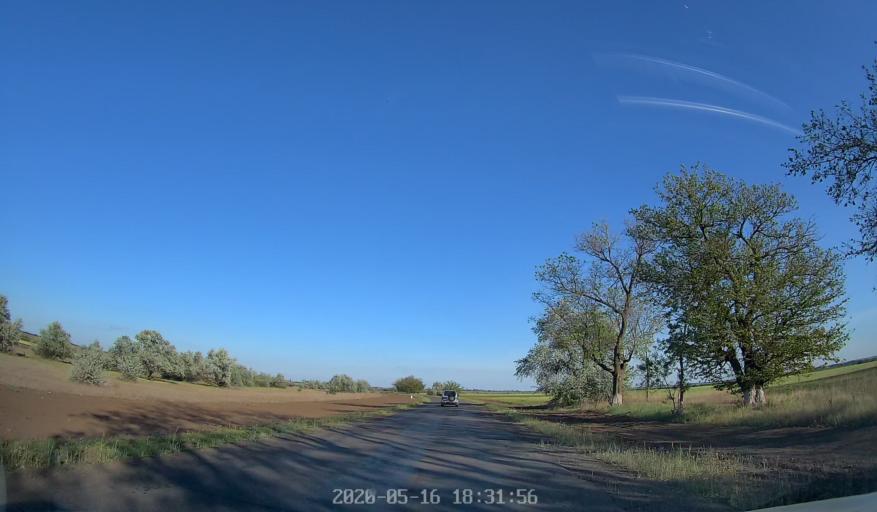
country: UA
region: Odessa
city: Lymanske
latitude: 46.5408
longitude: 30.0475
